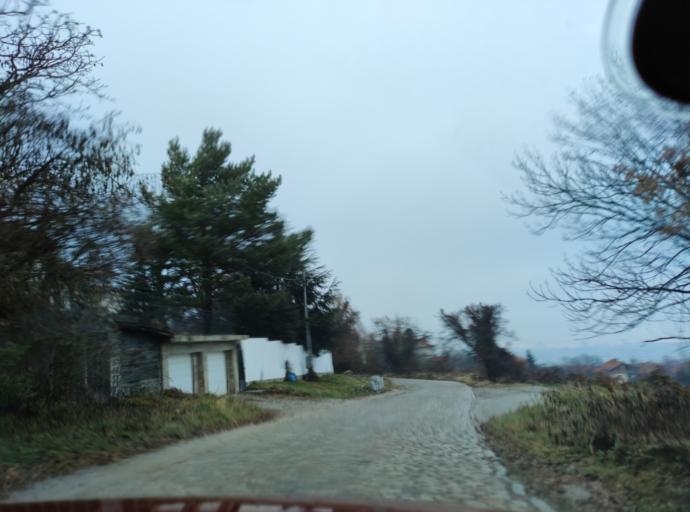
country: BG
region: Sofia-Capital
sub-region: Stolichna Obshtina
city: Sofia
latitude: 42.6236
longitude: 23.3090
